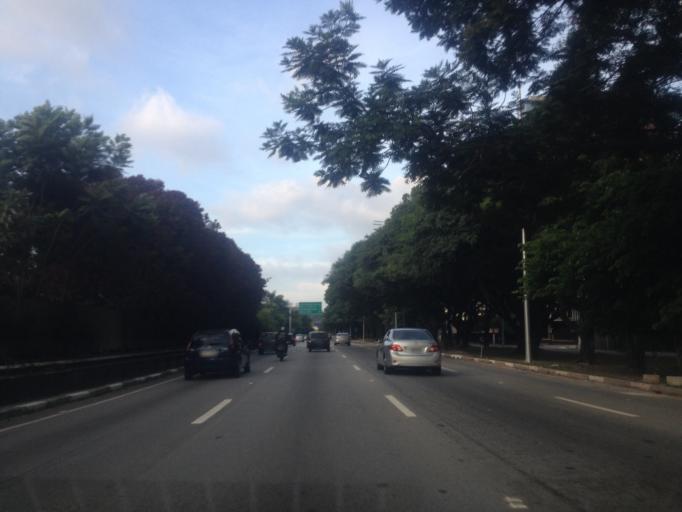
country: BR
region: Sao Paulo
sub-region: Taboao Da Serra
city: Taboao da Serra
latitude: -23.6321
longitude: -46.7158
